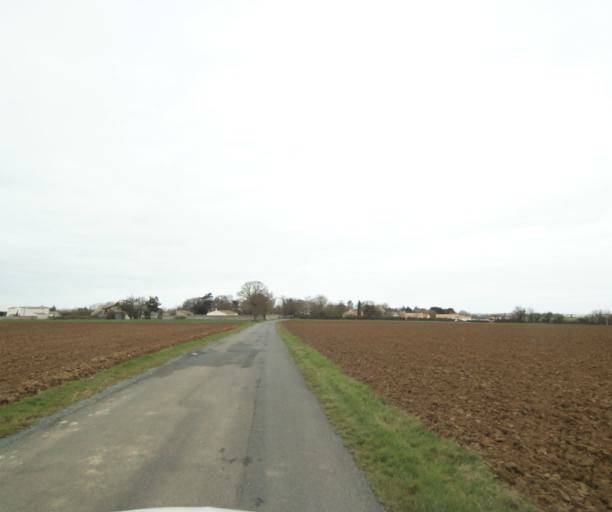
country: FR
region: Poitou-Charentes
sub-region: Departement de la Charente-Maritime
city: Nieul-sur-Mer
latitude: 46.1929
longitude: -1.1687
